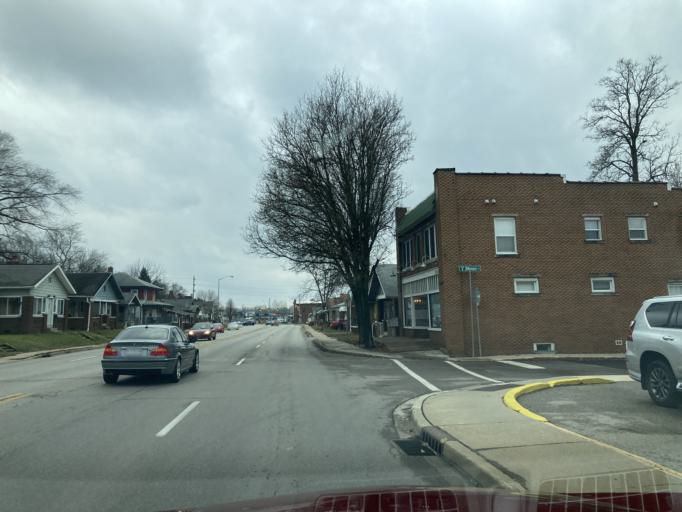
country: US
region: Indiana
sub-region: Monroe County
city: Bloomington
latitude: 39.1524
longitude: -86.5338
